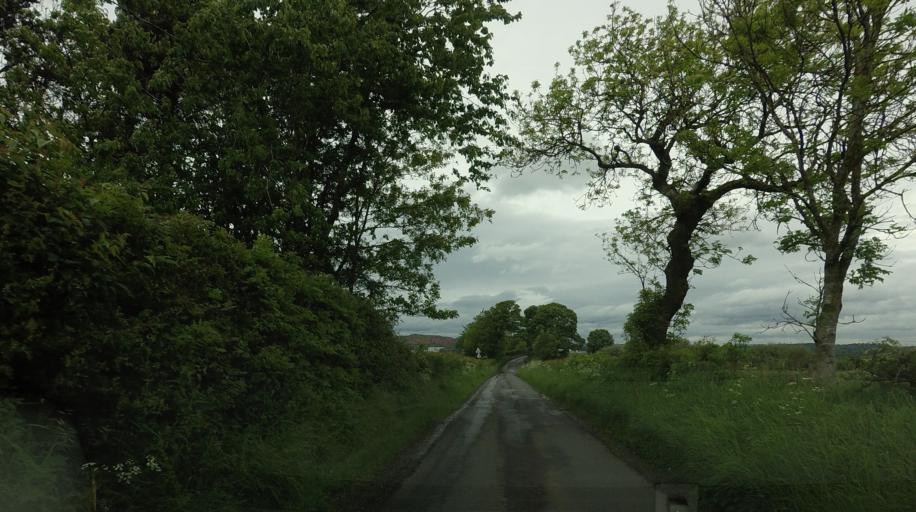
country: GB
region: Scotland
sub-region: West Lothian
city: Broxburn
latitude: 55.9227
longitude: -3.4448
